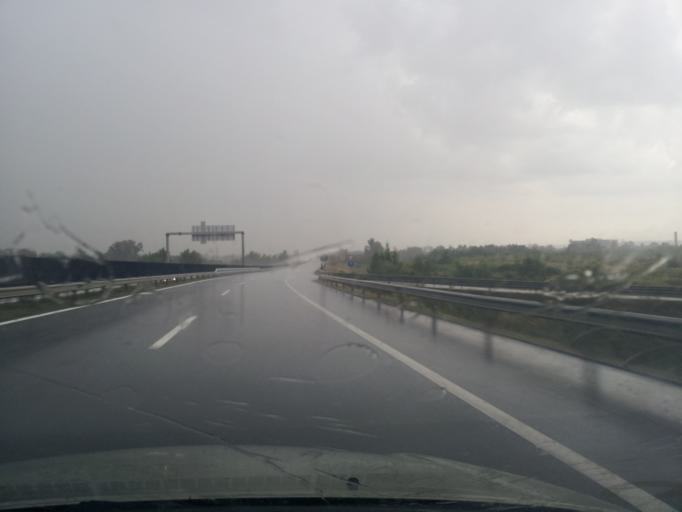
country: HU
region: Borsod-Abauj-Zemplen
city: Felsozsolca
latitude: 48.1061
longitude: 20.8451
